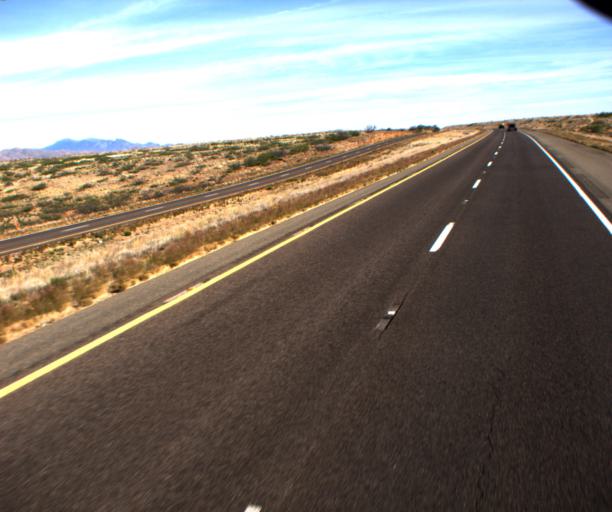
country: US
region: Arizona
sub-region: Cochise County
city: Willcox
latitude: 32.3993
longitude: -109.6622
